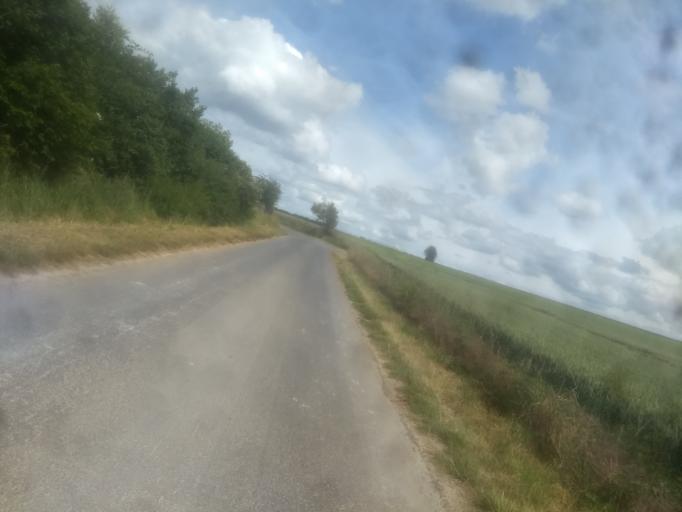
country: FR
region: Nord-Pas-de-Calais
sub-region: Departement du Pas-de-Calais
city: Duisans
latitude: 50.3042
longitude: 2.6758
